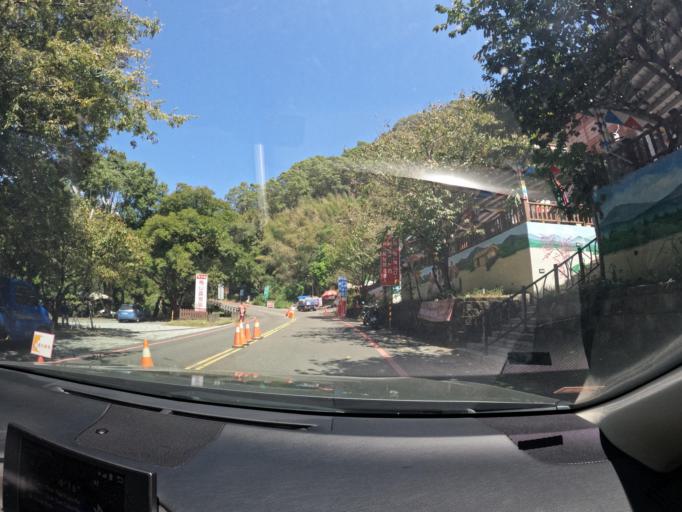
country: TW
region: Taiwan
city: Yujing
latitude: 23.2646
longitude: 120.8258
